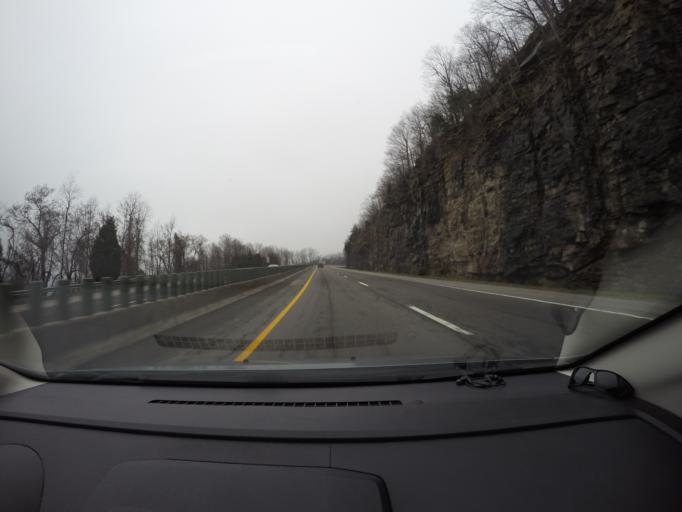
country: US
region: Tennessee
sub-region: Marion County
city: Monteagle
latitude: 35.2392
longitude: -85.8633
